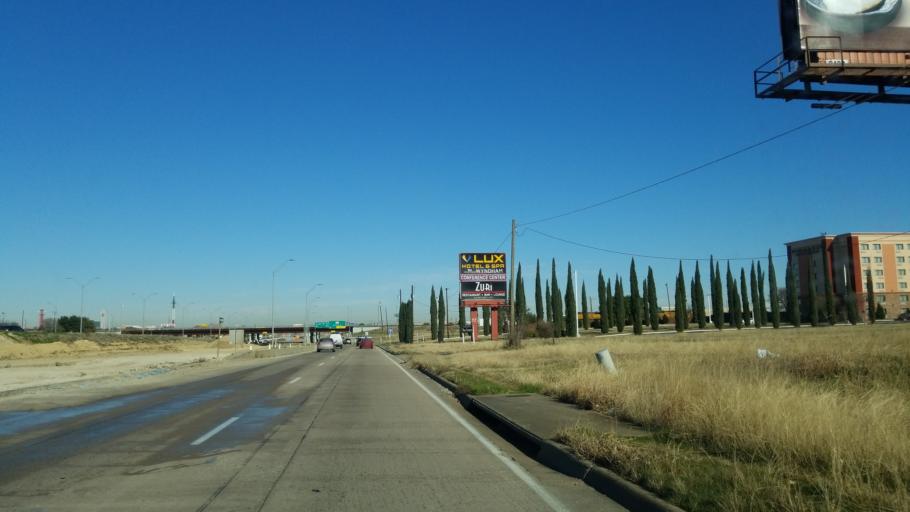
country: US
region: Texas
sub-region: Tarrant County
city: Arlington
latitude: 32.7390
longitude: -97.0618
